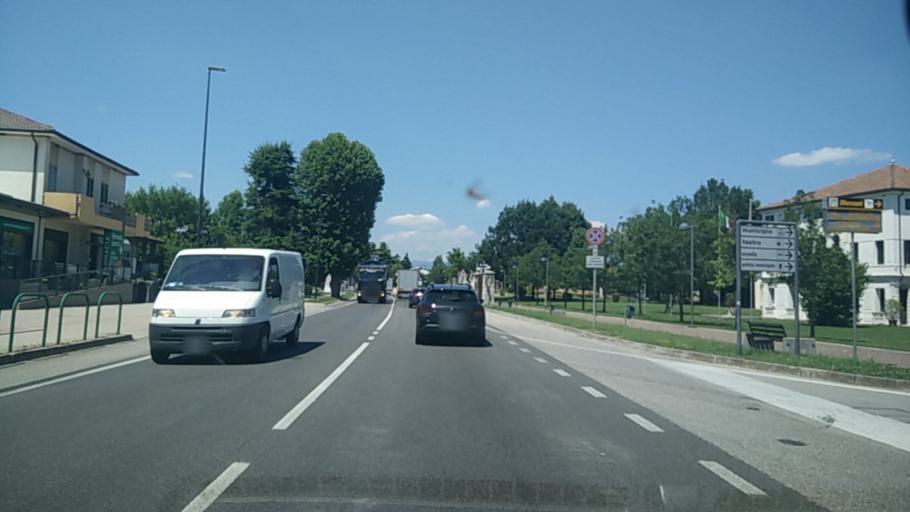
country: IT
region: Veneto
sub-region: Provincia di Padova
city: San Giorgio in Bosco
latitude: 45.5923
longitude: 11.8059
